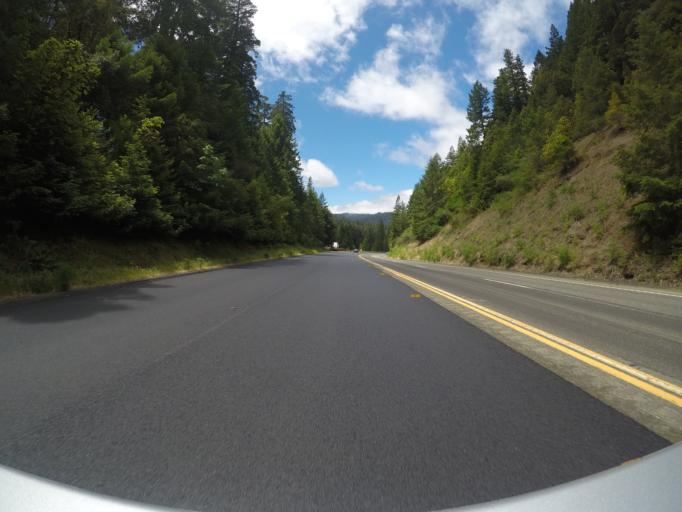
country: US
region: California
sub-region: Humboldt County
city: Redway
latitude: 40.2854
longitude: -123.8912
